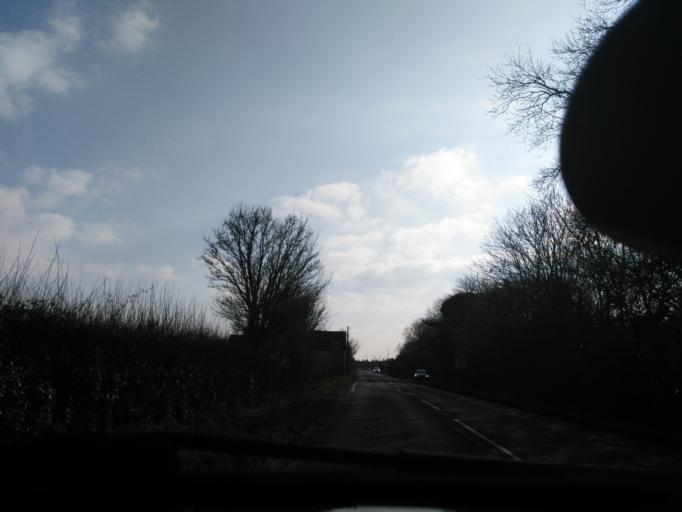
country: GB
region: England
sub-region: Wiltshire
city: Norton
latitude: 51.5286
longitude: -2.1244
